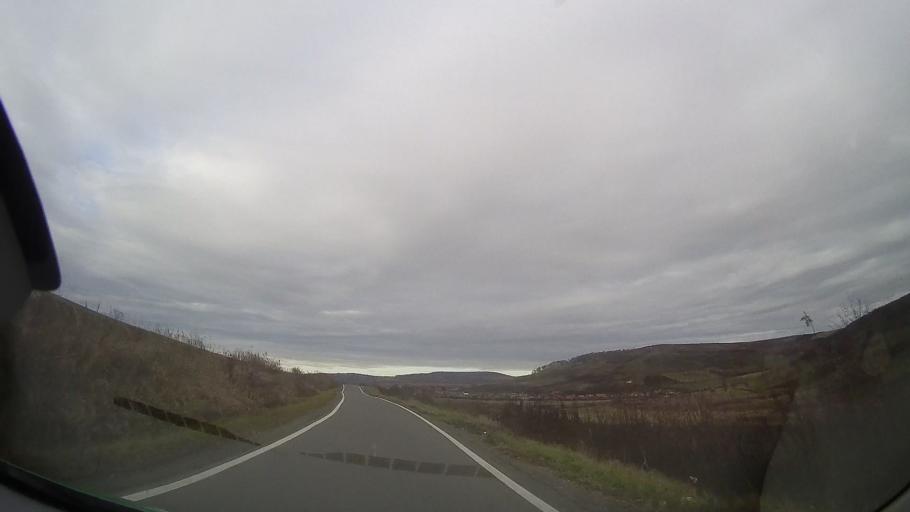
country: RO
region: Mures
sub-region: Comuna Faragau
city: Faragau
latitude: 46.7696
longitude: 24.5576
